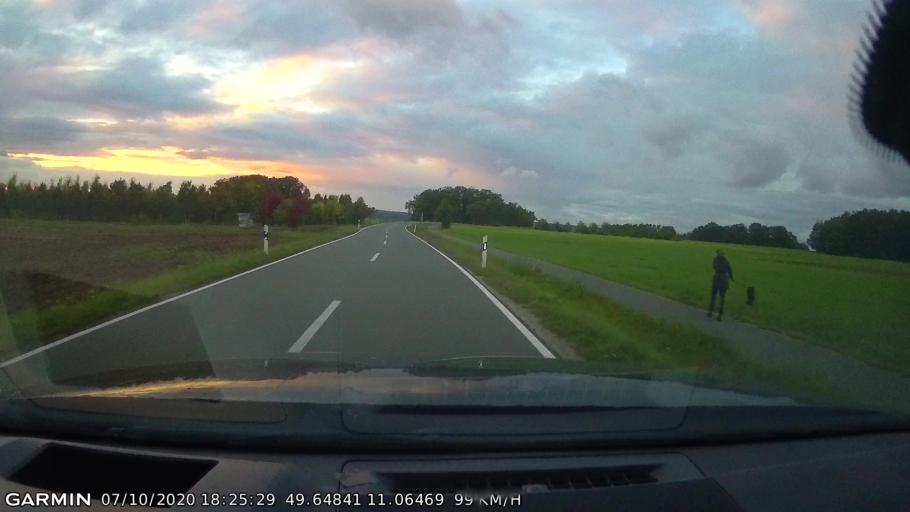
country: DE
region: Bavaria
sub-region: Upper Franconia
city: Langensendelbach
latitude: 49.6484
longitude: 11.0647
